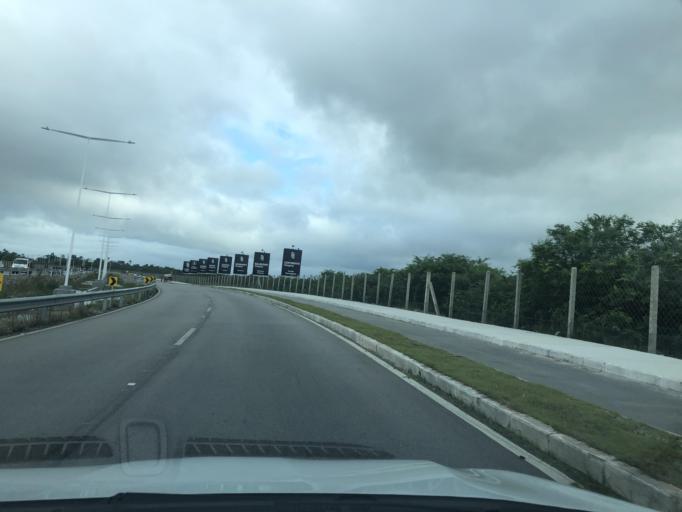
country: BR
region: Santa Catarina
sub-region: Florianopolis
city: Carianos
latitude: -27.6756
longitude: -48.5274
